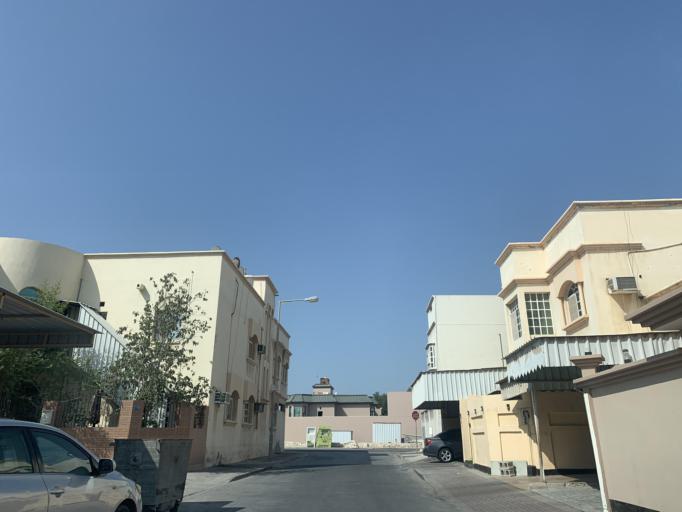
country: BH
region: Central Governorate
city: Madinat Hamad
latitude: 26.1385
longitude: 50.5059
